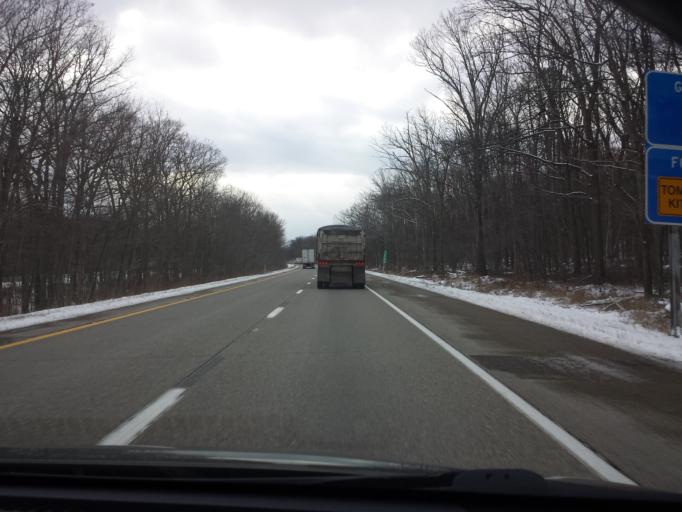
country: US
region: Pennsylvania
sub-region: Luzerne County
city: Conyngham
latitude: 41.0335
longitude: -76.0631
